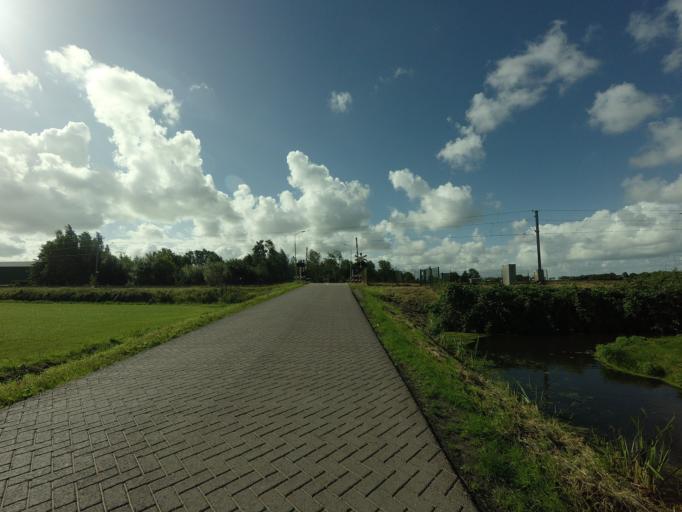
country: NL
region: North Holland
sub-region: Gemeente Hoorn
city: Hoorn
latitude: 52.6559
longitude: 4.9993
